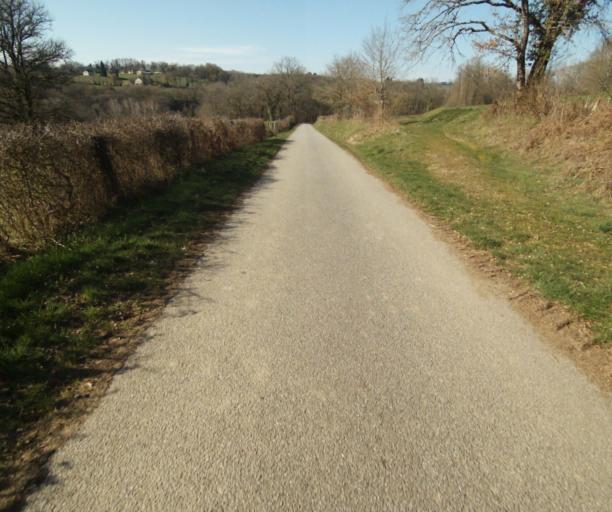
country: FR
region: Limousin
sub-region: Departement de la Correze
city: Chamboulive
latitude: 45.4825
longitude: 1.6865
